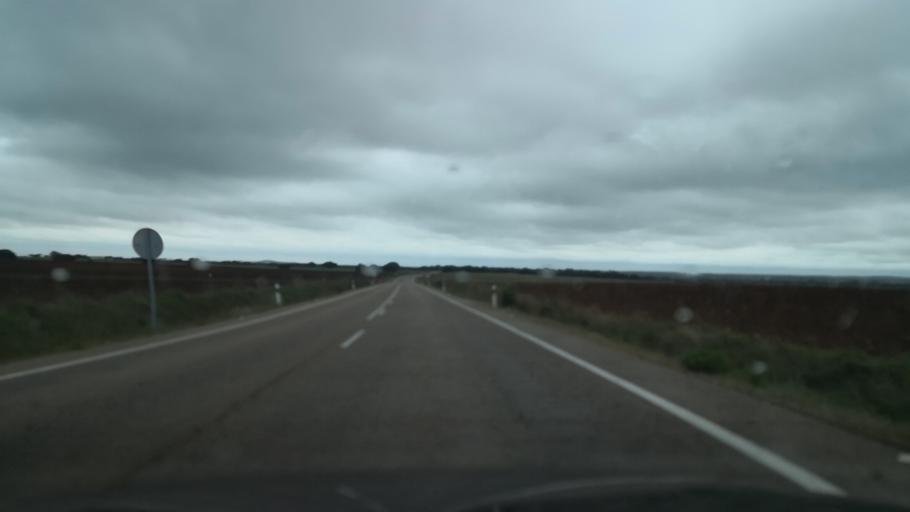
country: ES
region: Extremadura
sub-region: Provincia de Badajoz
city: Villar del Rey
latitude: 39.0525
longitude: -6.7979
